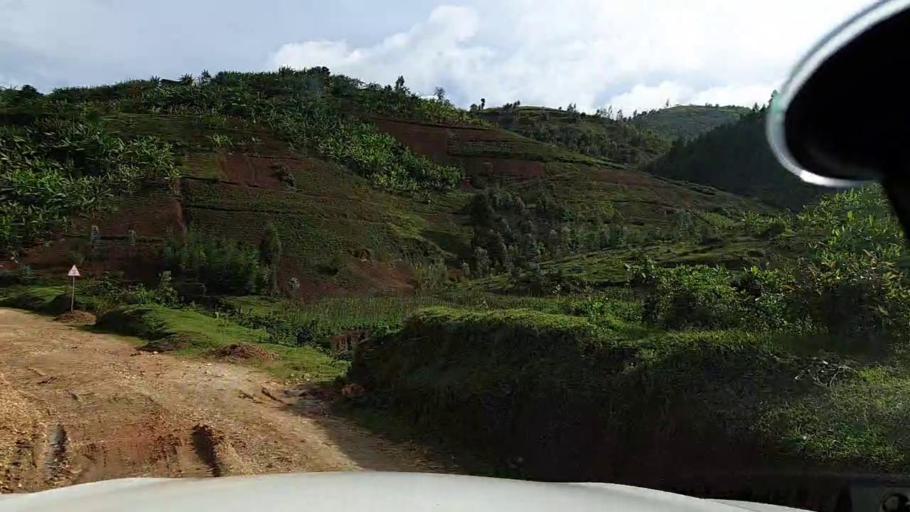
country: RW
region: Western Province
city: Kibuye
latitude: -2.1290
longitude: 29.4985
